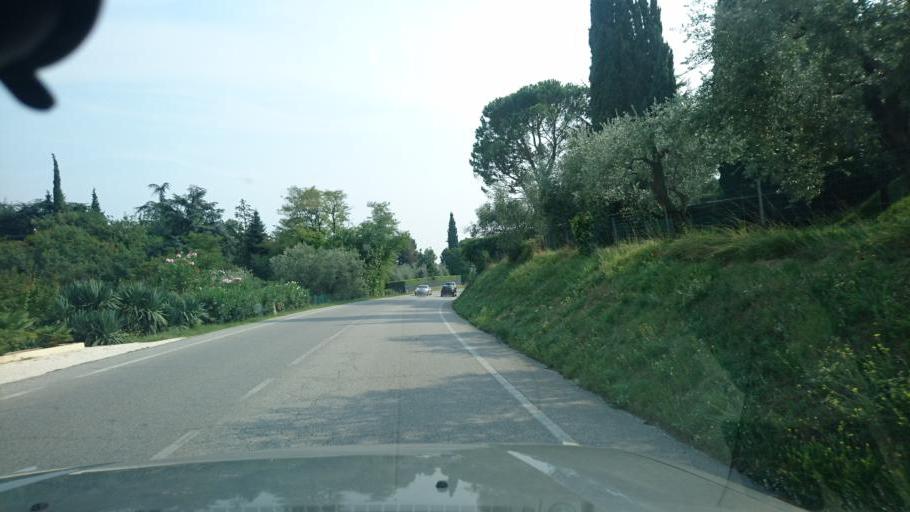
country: IT
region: Lombardy
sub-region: Provincia di Brescia
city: Cunettone-Villa
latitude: 45.5993
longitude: 10.5030
